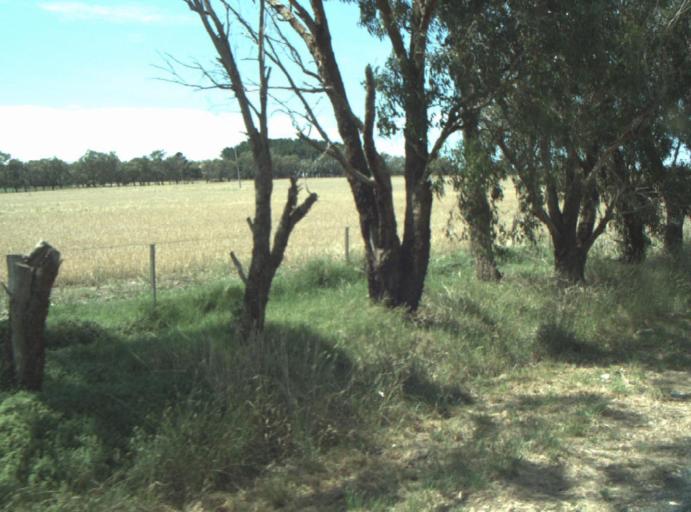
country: AU
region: Victoria
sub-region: Greater Geelong
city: Leopold
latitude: -38.1706
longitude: 144.4719
